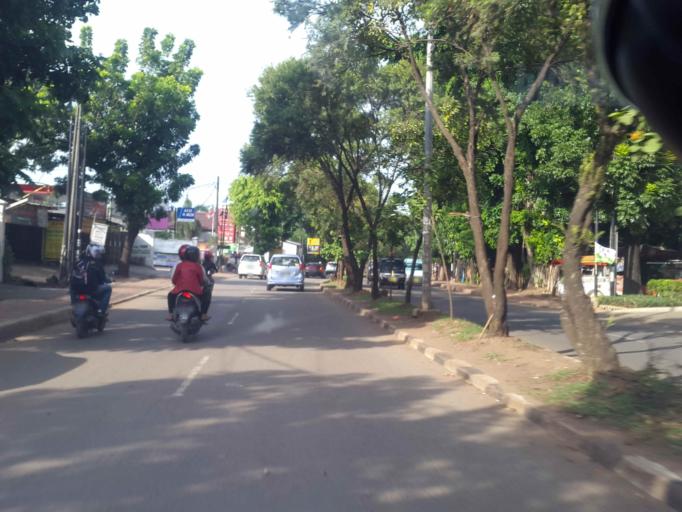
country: ID
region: West Java
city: Bekasi
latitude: -6.2432
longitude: 106.9202
